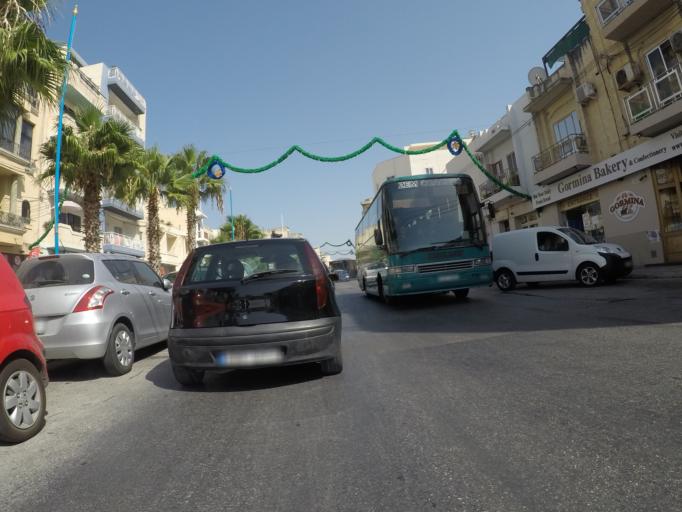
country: MT
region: Saint Paul's Bay
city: San Pawl il-Bahar
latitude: 35.9471
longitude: 14.4078
